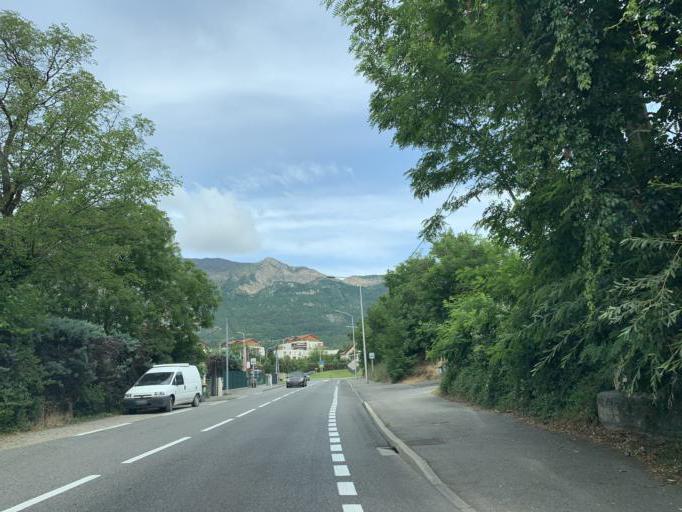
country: FR
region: Provence-Alpes-Cote d'Azur
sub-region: Departement des Hautes-Alpes
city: Gap
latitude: 44.5562
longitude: 6.0646
